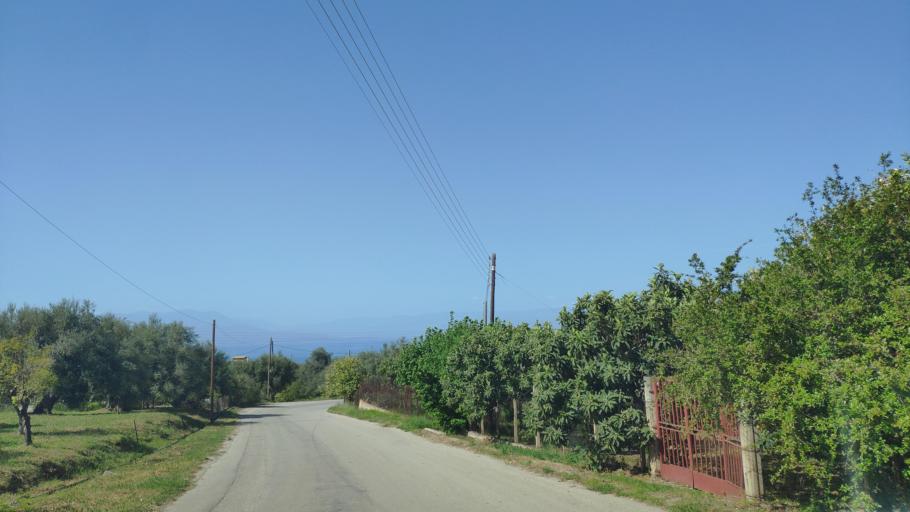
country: GR
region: West Greece
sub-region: Nomos Achaias
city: Aiyira
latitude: 38.1406
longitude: 22.3494
